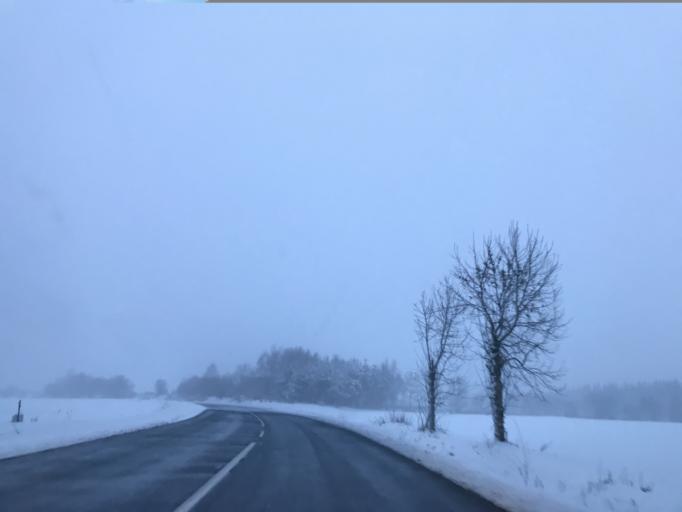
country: FR
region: Auvergne
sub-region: Departement du Puy-de-Dome
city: Saint-Sauves-d'Auvergne
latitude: 45.6532
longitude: 2.6999
